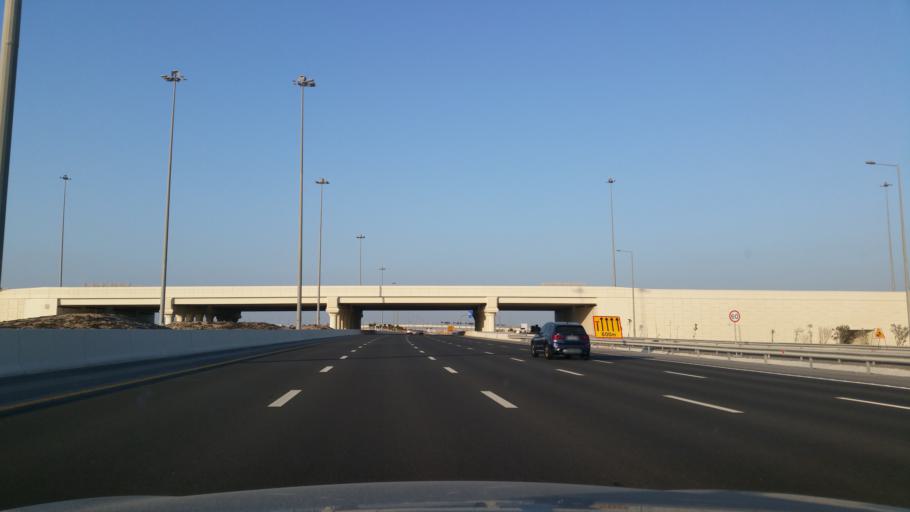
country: QA
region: Al Khawr
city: Al Khawr
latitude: 25.6396
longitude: 51.4925
